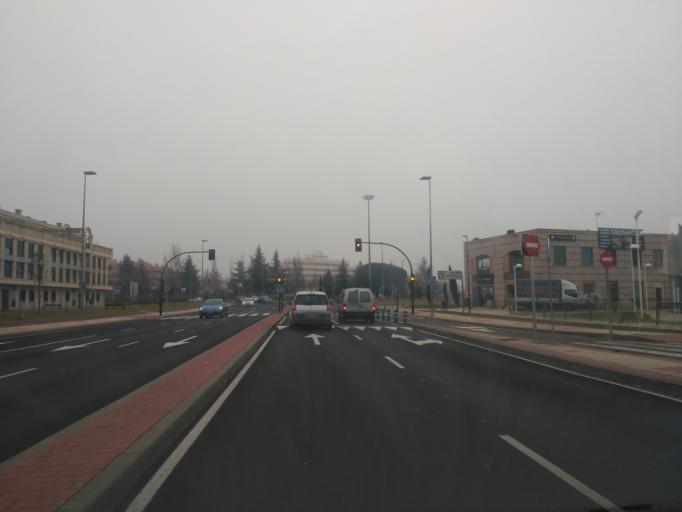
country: ES
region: Castille and Leon
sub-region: Provincia de Salamanca
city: Santa Marta de Tormes
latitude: 40.9519
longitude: -5.6409
